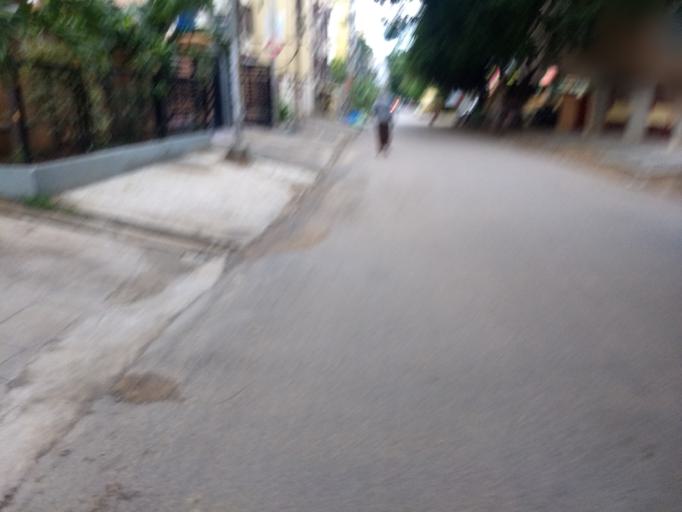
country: IN
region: Telangana
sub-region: Rangareddi
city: Kukatpalli
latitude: 17.4894
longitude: 78.3836
